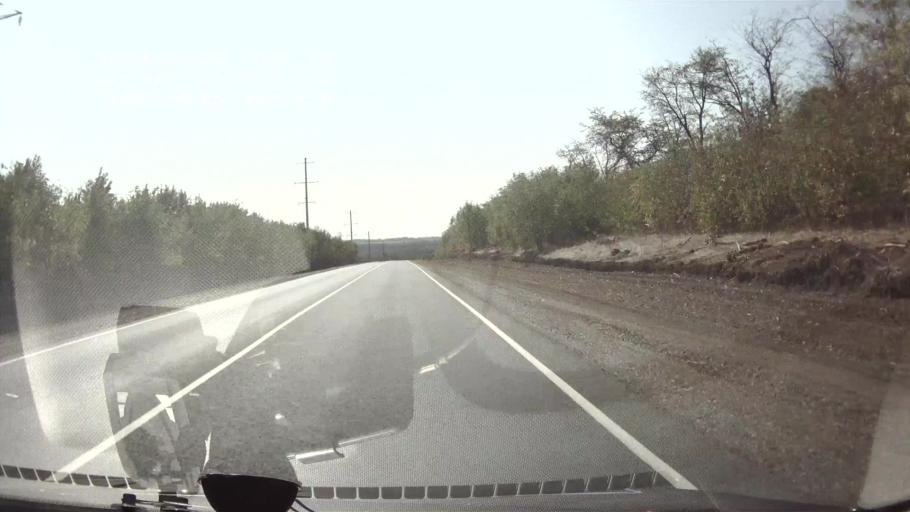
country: RU
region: Krasnodarskiy
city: Kavkazskaya
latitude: 45.5552
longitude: 40.6929
